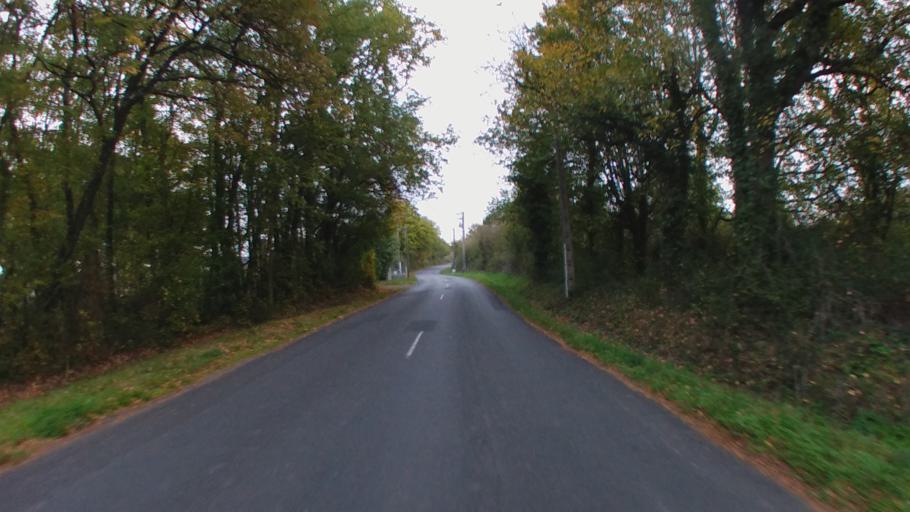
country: FR
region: Pays de la Loire
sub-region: Departement de Maine-et-Loire
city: Saumur
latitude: 47.2596
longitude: -0.1177
